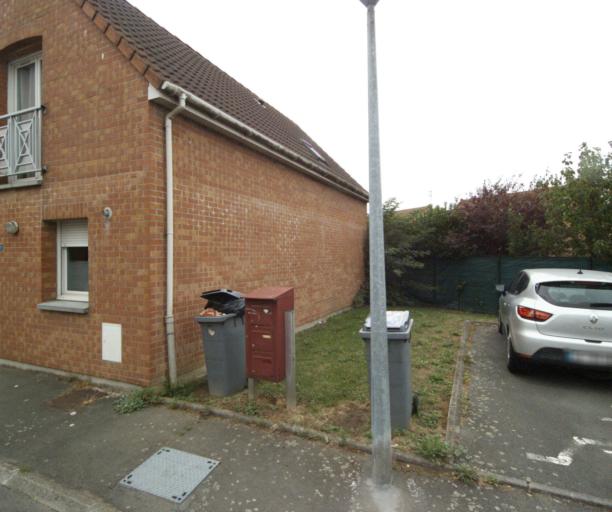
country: FR
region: Nord-Pas-de-Calais
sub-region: Departement du Nord
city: Leers
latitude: 50.6874
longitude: 3.2324
